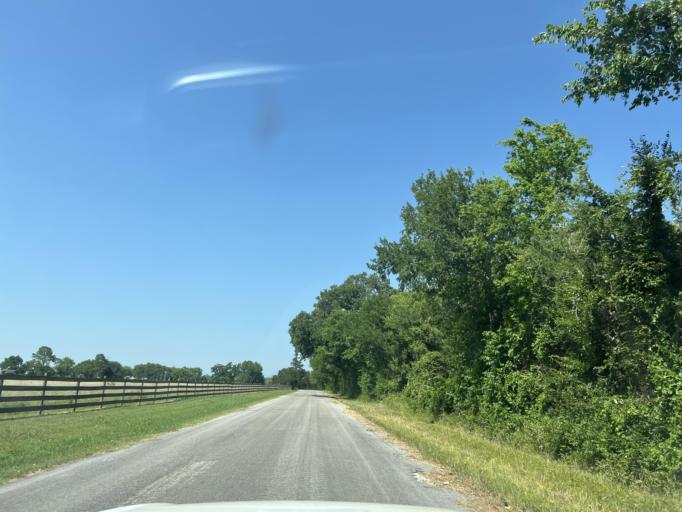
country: US
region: Texas
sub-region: Washington County
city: Brenham
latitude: 30.1713
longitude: -96.5119
